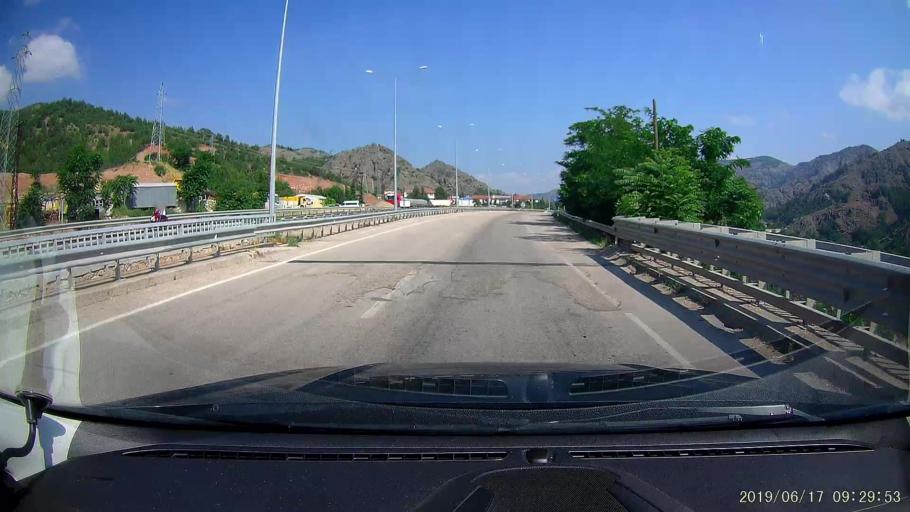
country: TR
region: Amasya
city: Amasya
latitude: 40.7001
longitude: 35.8070
